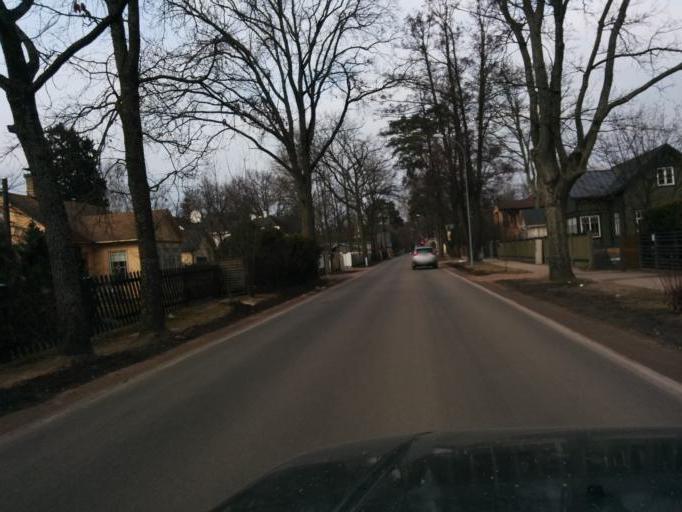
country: LV
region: Jurmala
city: Jurmala
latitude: 56.9603
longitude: 23.7226
